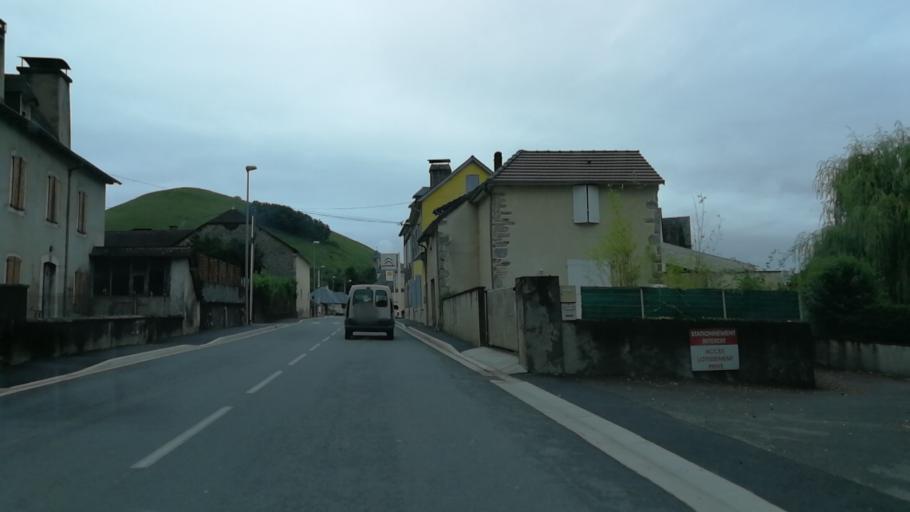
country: FR
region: Aquitaine
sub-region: Departement des Pyrenees-Atlantiques
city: Oloron-Sainte-Marie
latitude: 43.1194
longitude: -0.6138
